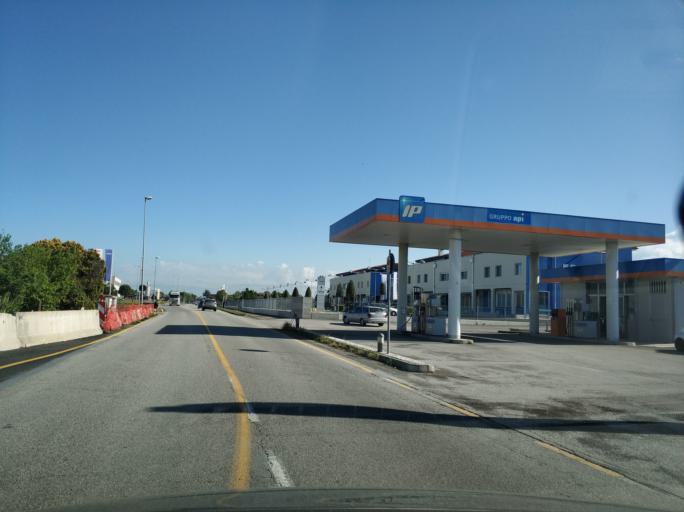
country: IT
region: Friuli Venezia Giulia
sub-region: Provincia di Udine
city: Porpetto
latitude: 45.8477
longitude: 13.2125
